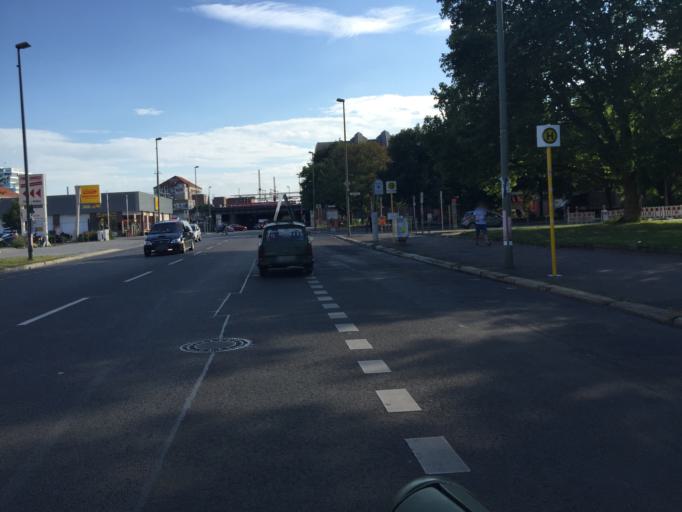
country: DE
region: Berlin
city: Friedrichshain Bezirk
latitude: 52.5115
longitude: 13.4379
